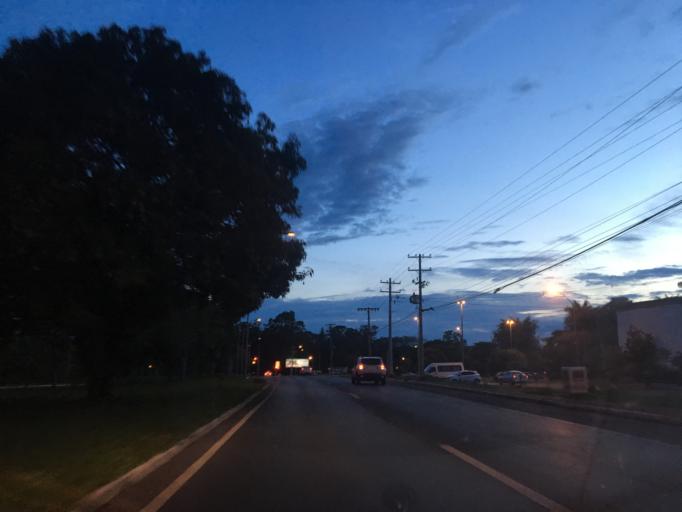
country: BR
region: Federal District
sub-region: Brasilia
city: Brasilia
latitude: -15.8525
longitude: -47.8765
